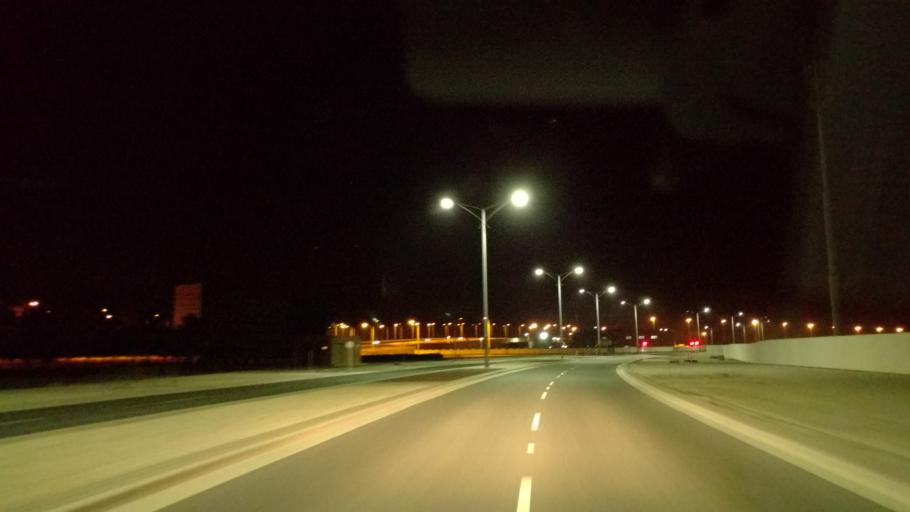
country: AE
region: Abu Dhabi
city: Abu Dhabi
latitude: 24.5450
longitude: 54.4501
